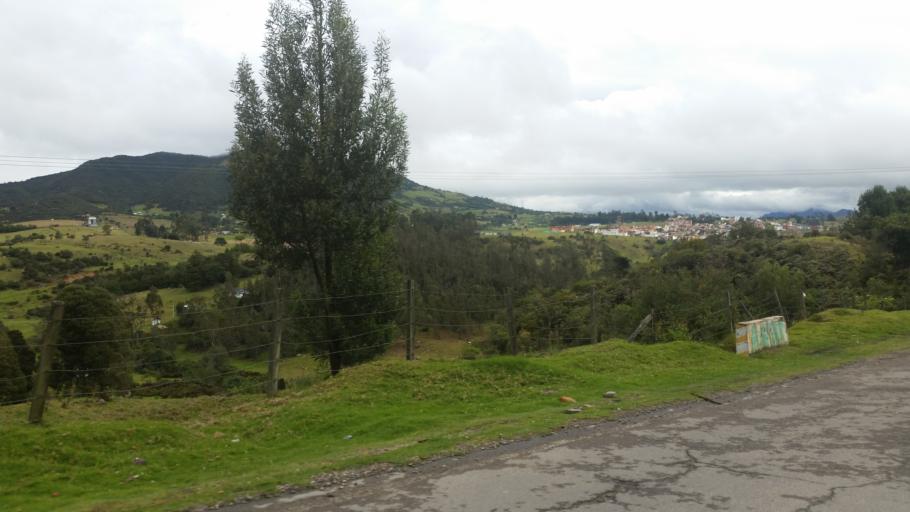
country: CO
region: Cundinamarca
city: La Calera
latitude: 4.7079
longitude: -73.9738
